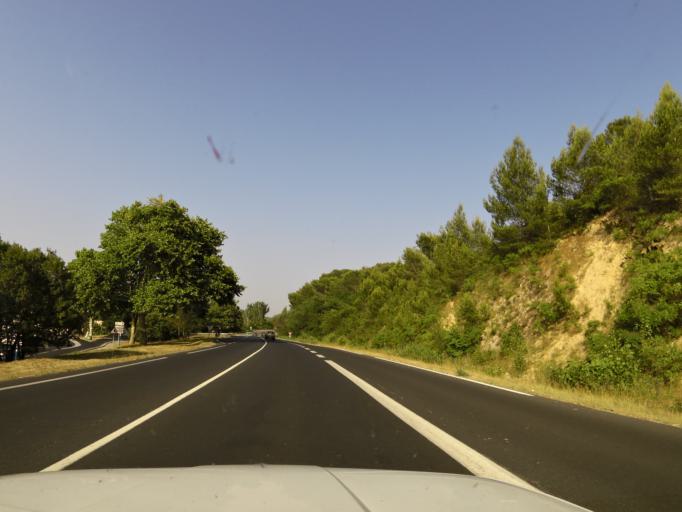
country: FR
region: Languedoc-Roussillon
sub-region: Departement de l'Herault
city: Castelnau-le-Lez
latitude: 43.6433
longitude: 3.8965
